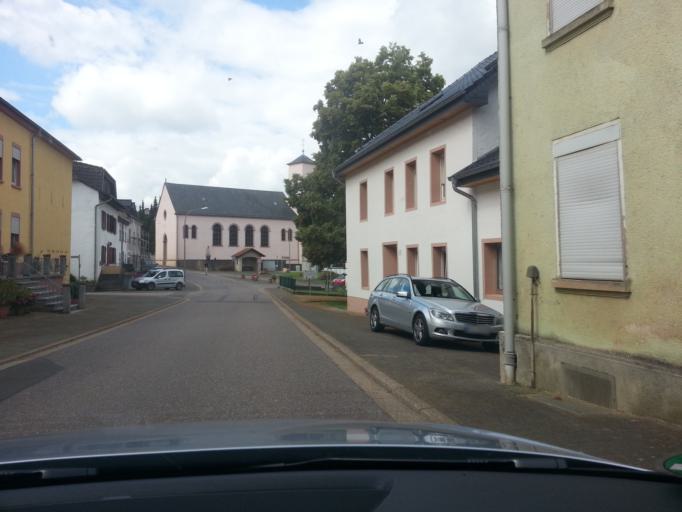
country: DE
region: Rheinland-Pfalz
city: Kirf
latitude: 49.5327
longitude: 6.4327
